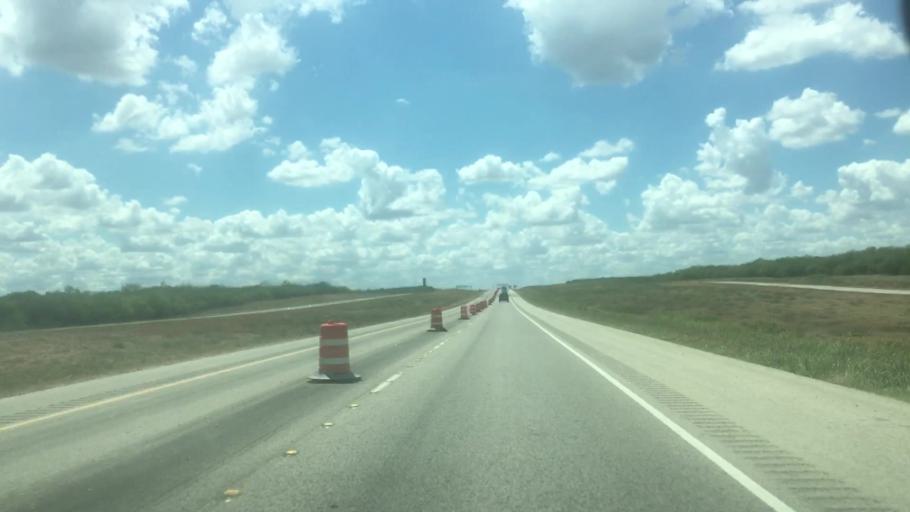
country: US
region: Texas
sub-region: Caldwell County
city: Martindale
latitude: 29.8222
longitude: -97.7525
